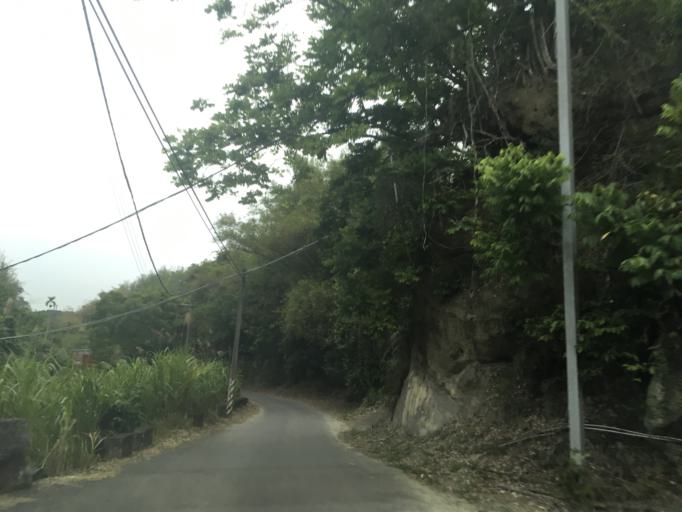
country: TW
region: Taiwan
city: Zhongxing New Village
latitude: 24.0380
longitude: 120.7574
